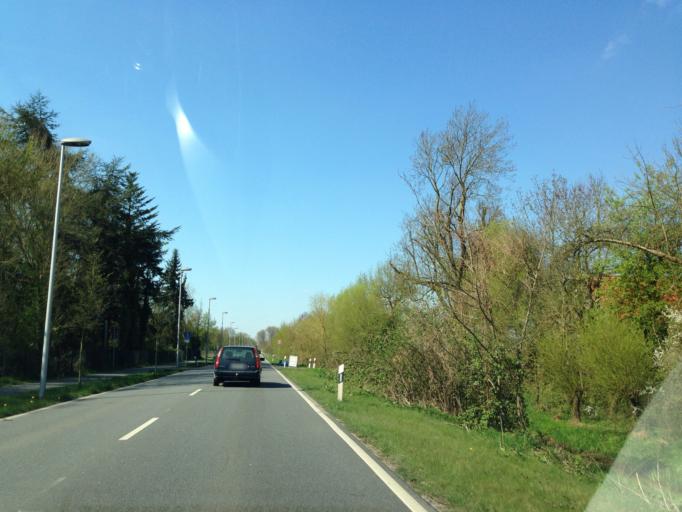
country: DE
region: North Rhine-Westphalia
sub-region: Regierungsbezirk Munster
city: Muenster
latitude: 51.9865
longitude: 7.6274
